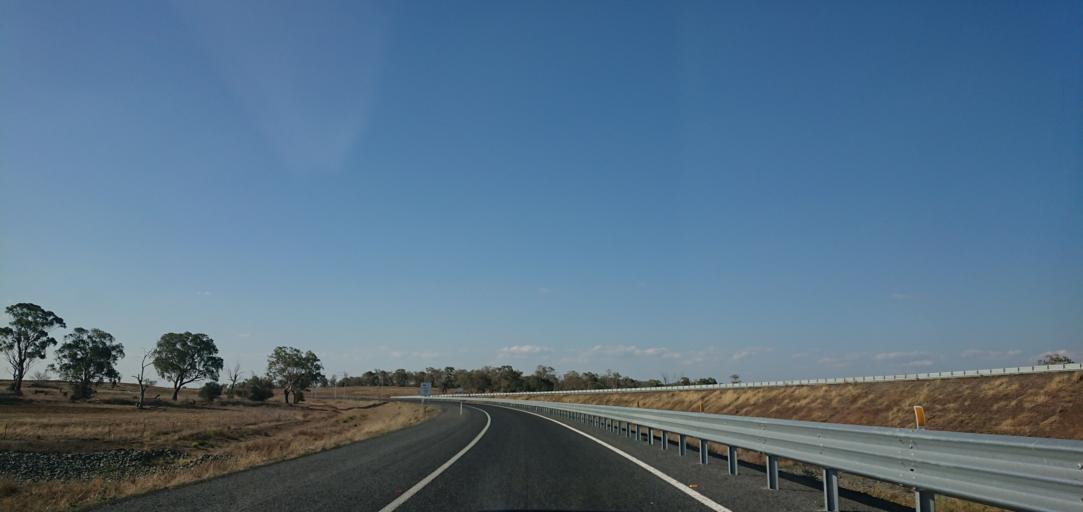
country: AU
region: Queensland
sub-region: Toowoomba
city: Westbrook
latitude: -27.6133
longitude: 151.7855
